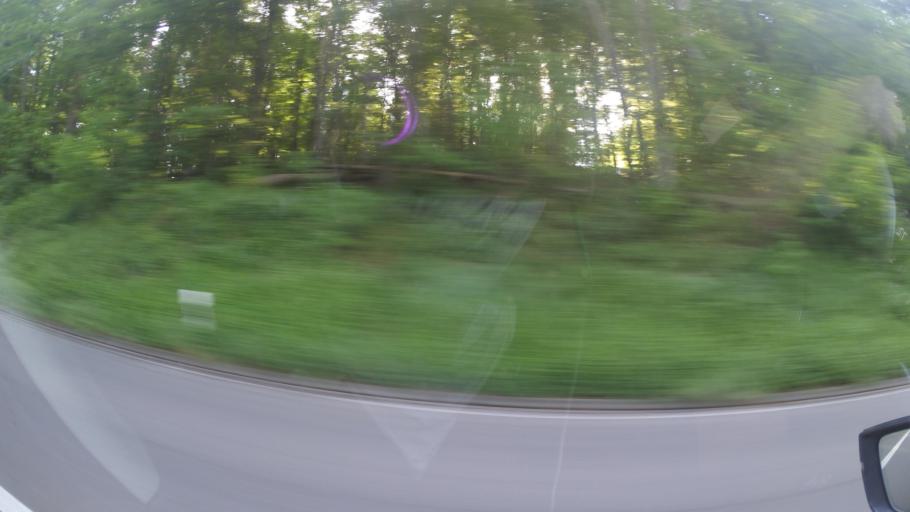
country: DE
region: Rheinland-Pfalz
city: Waldrohrbach
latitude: 49.1794
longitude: 7.9533
